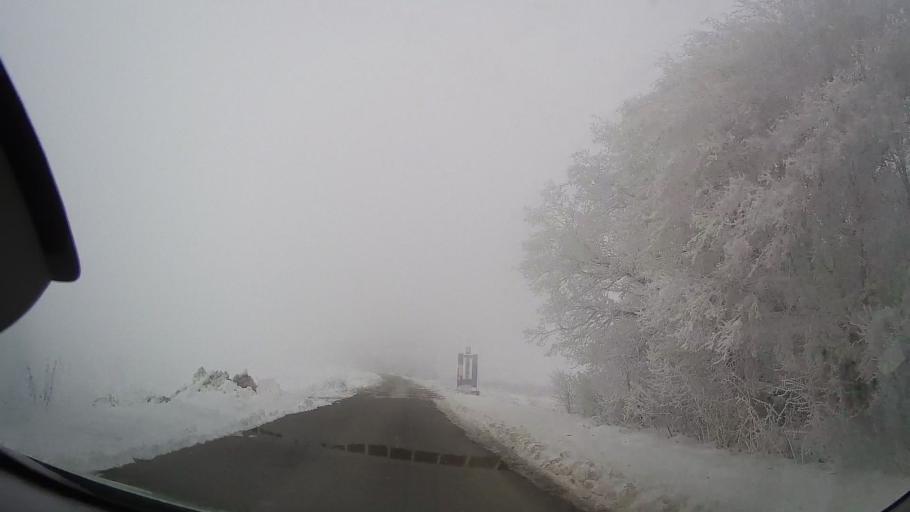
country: RO
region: Iasi
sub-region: Comuna Dagata
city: Dagata
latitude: 46.9215
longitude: 27.1764
